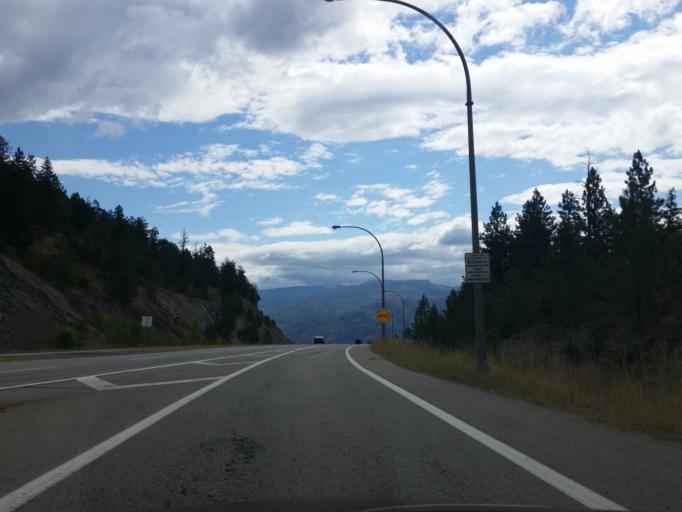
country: CA
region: British Columbia
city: Peachland
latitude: 49.8033
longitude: -119.7104
